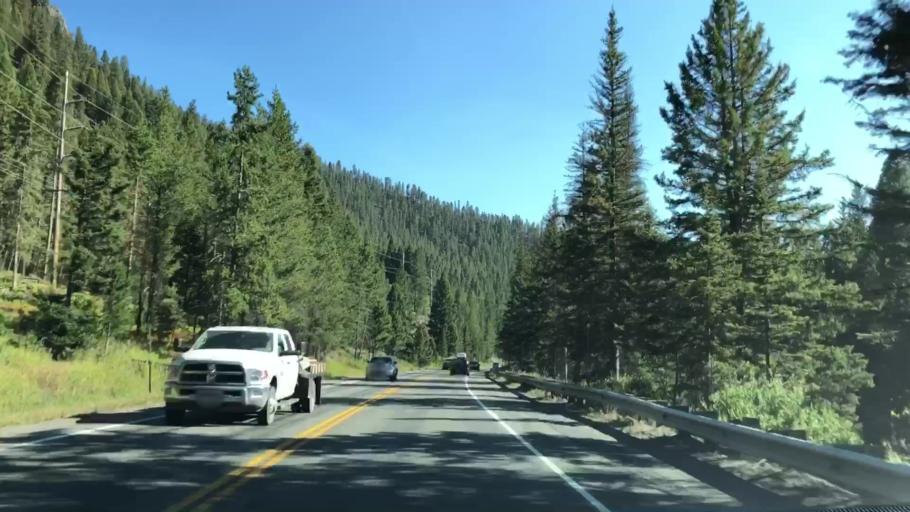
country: US
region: Montana
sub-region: Gallatin County
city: Big Sky
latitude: 45.3620
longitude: -111.1718
